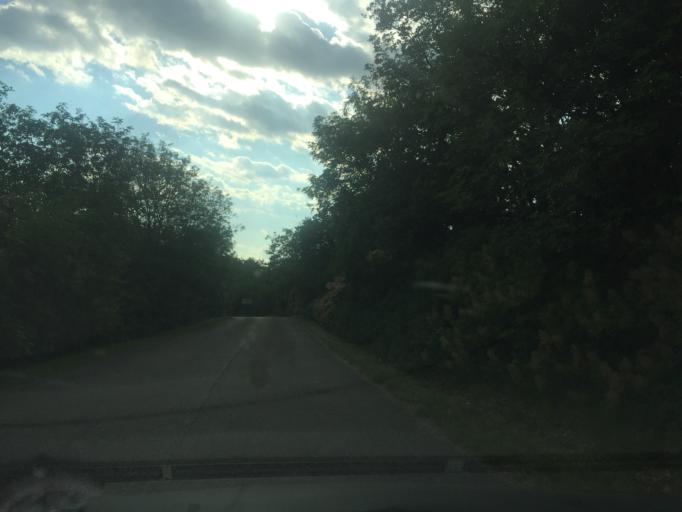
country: IT
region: Friuli Venezia Giulia
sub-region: Provincia di Gorizia
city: Doberdo del Lago
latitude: 45.8755
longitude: 13.5410
